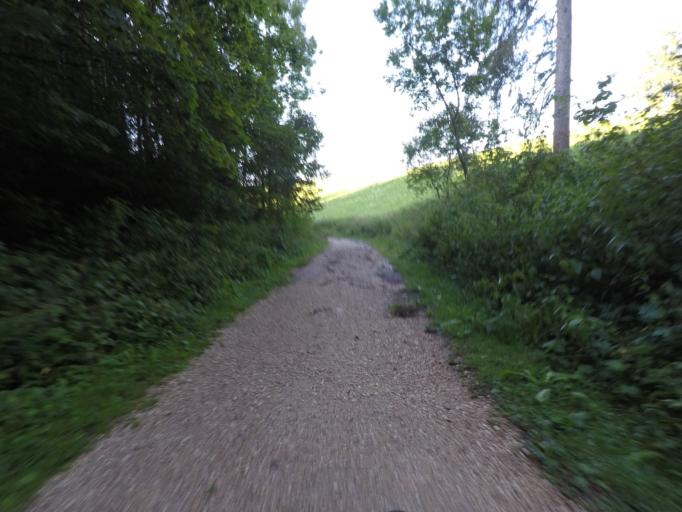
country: IT
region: Veneto
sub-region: Provincia di Vicenza
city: Asiago
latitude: 45.8615
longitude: 11.5273
